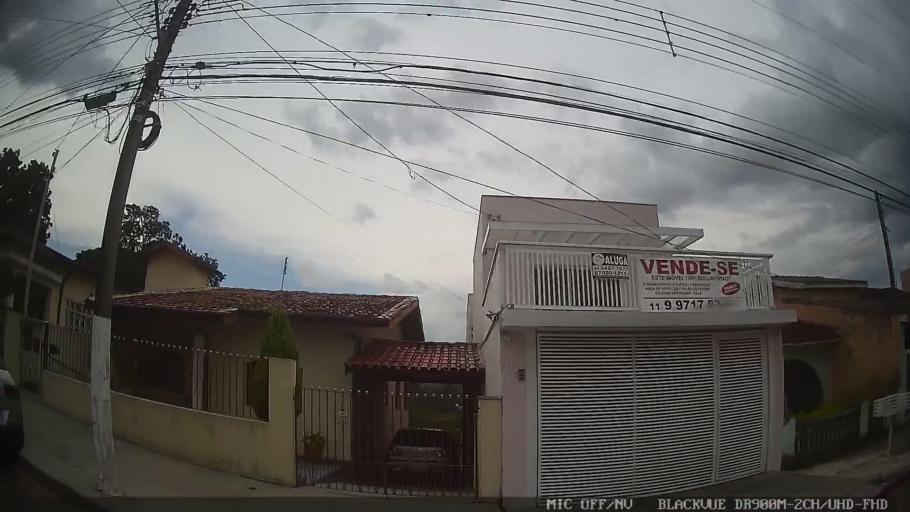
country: BR
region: Sao Paulo
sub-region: Atibaia
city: Atibaia
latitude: -23.1123
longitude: -46.5516
